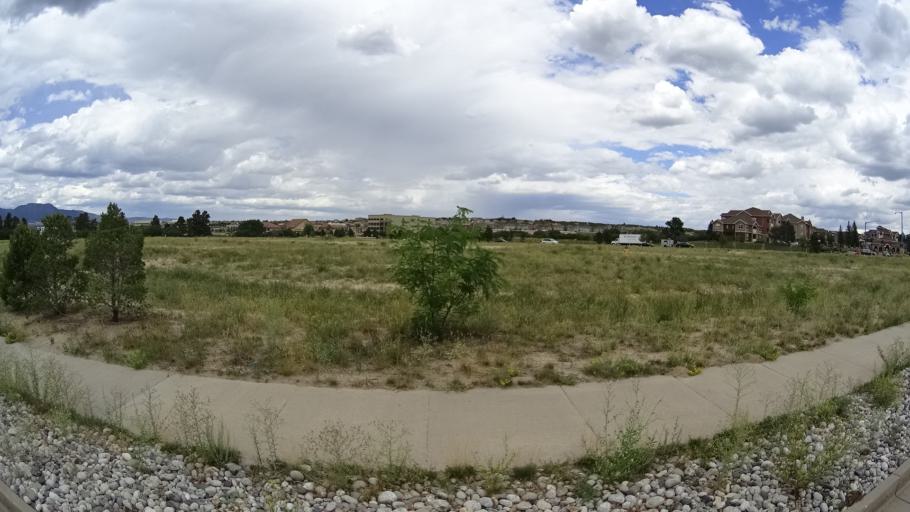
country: US
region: Colorado
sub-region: El Paso County
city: Gleneagle
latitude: 39.0172
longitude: -104.8133
